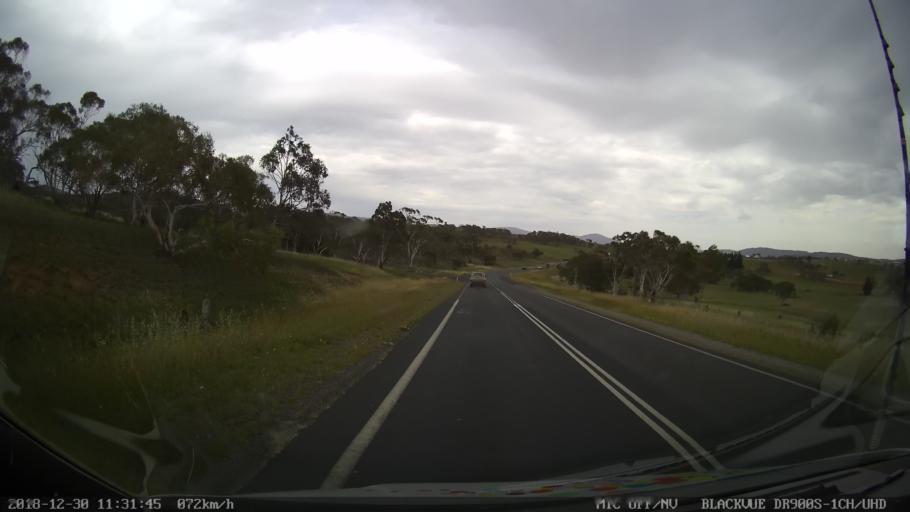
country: AU
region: New South Wales
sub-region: Snowy River
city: Jindabyne
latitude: -36.4286
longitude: 148.6096
